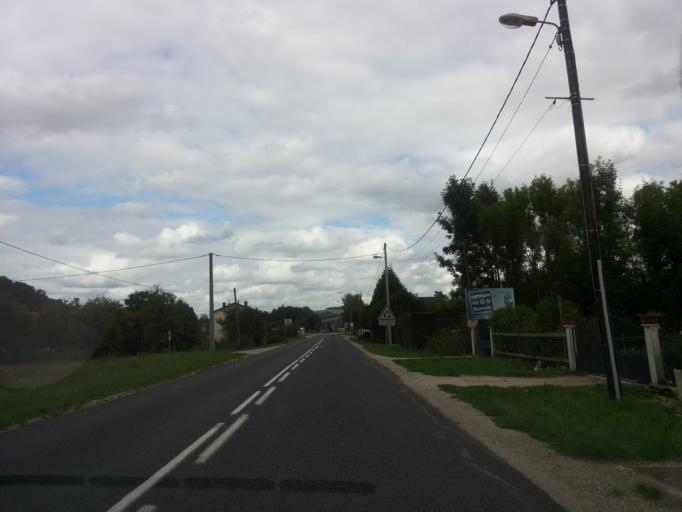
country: FR
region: Lorraine
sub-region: Departement de la Meuse
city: Ligny-en-Barrois
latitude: 48.6736
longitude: 5.3259
